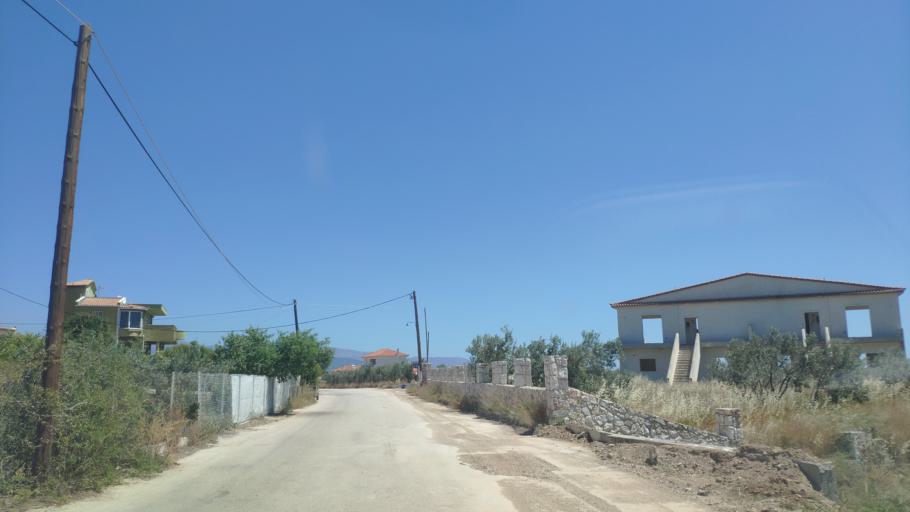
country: GR
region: Peloponnese
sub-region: Nomos Korinthias
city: Loutra Oraias Elenis
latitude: 37.8526
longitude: 22.9863
